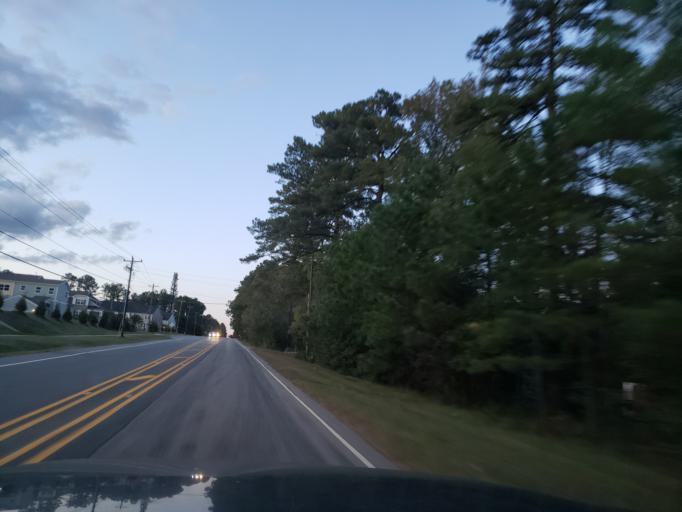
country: US
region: North Carolina
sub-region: Orange County
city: Chapel Hill
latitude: 35.8893
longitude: -78.9574
